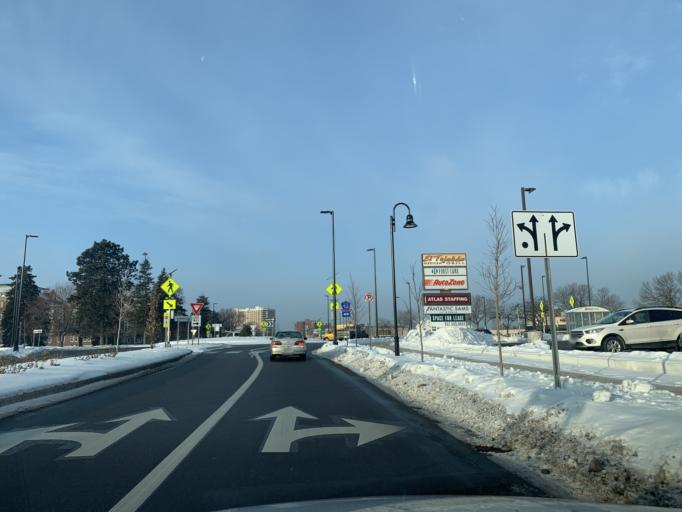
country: US
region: Minnesota
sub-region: Hennepin County
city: Richfield
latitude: 44.8835
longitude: -93.2773
